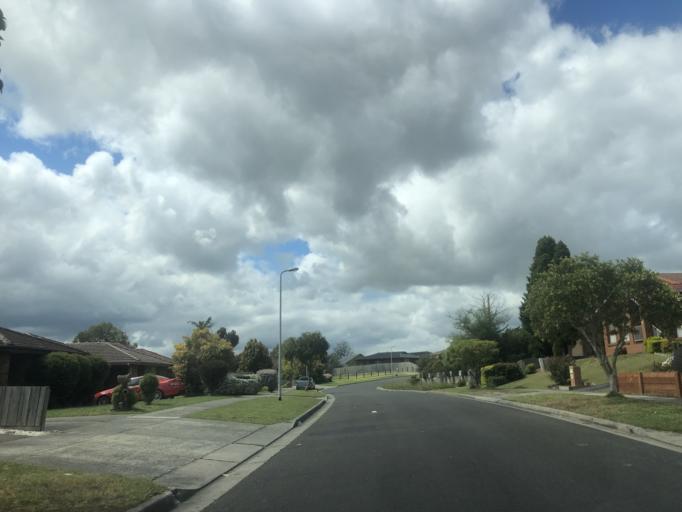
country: AU
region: Victoria
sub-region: Casey
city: Endeavour Hills
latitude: -37.9713
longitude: 145.2555
